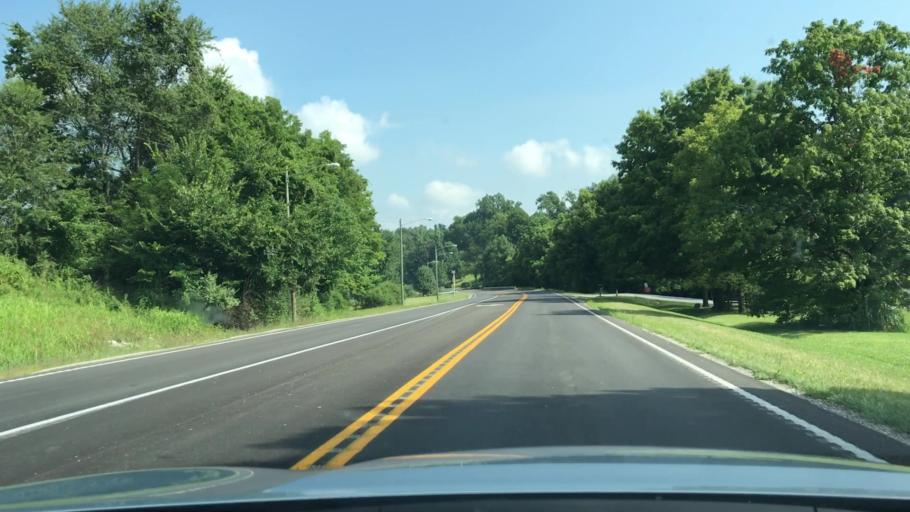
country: US
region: Kentucky
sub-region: Barren County
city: Glasgow
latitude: 37.0224
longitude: -85.9060
